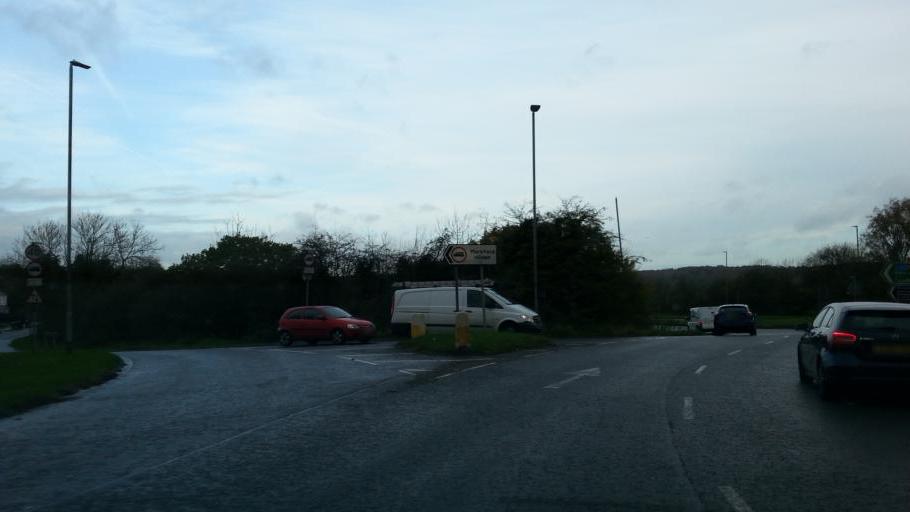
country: GB
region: England
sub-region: Leicestershire
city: Markfield
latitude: 52.6868
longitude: -1.2677
